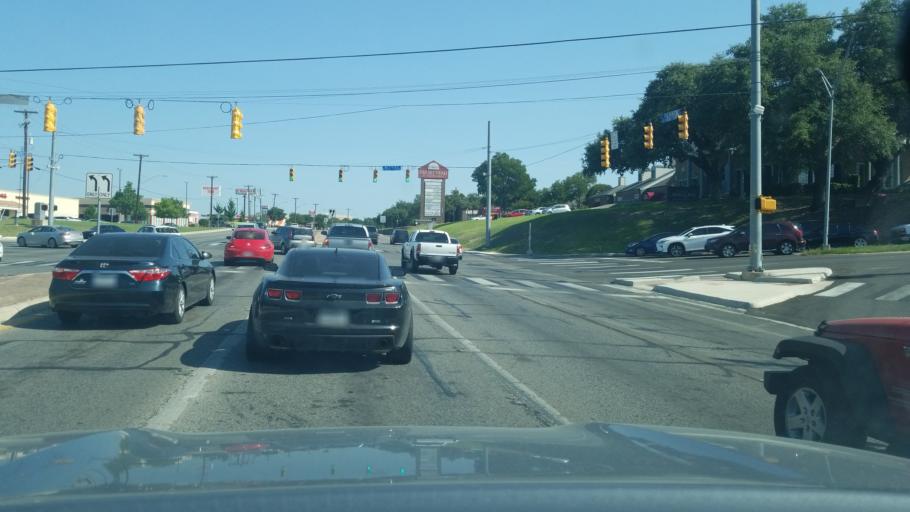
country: US
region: Texas
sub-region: Bexar County
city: Hollywood Park
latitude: 29.5795
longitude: -98.5146
